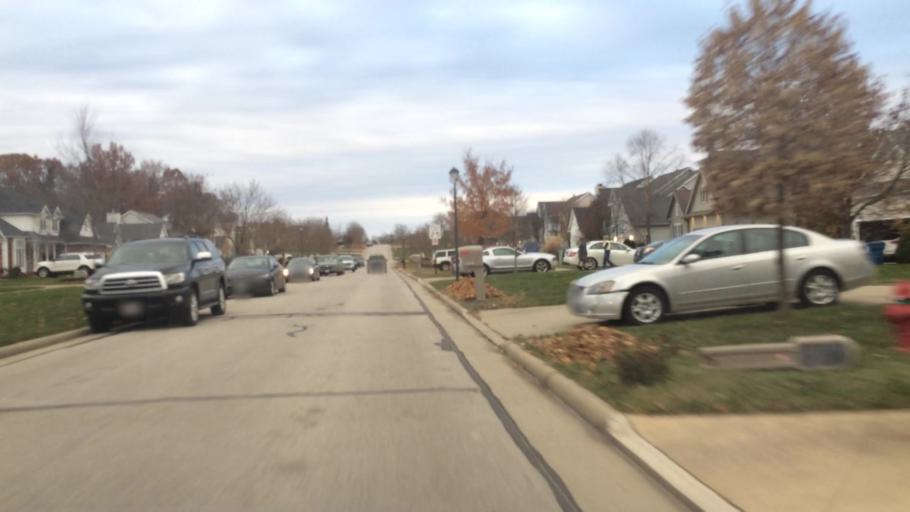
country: US
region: Ohio
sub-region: Portage County
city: Kent
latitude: 41.1677
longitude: -81.3875
